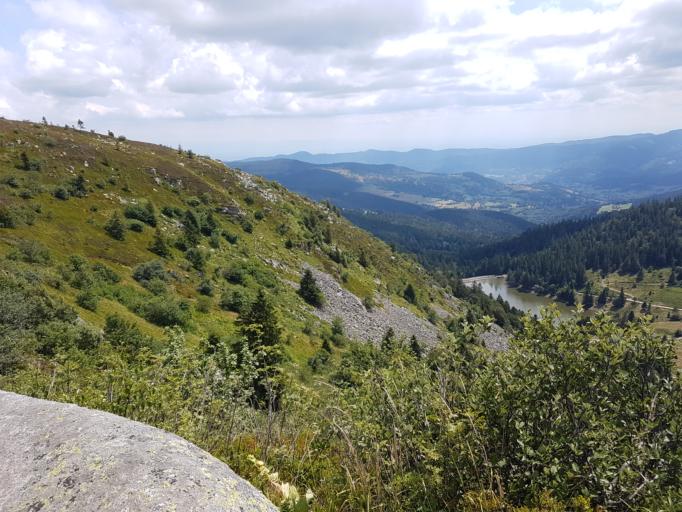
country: FR
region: Alsace
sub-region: Departement du Haut-Rhin
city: Soultzeren
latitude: 48.1081
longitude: 7.0724
